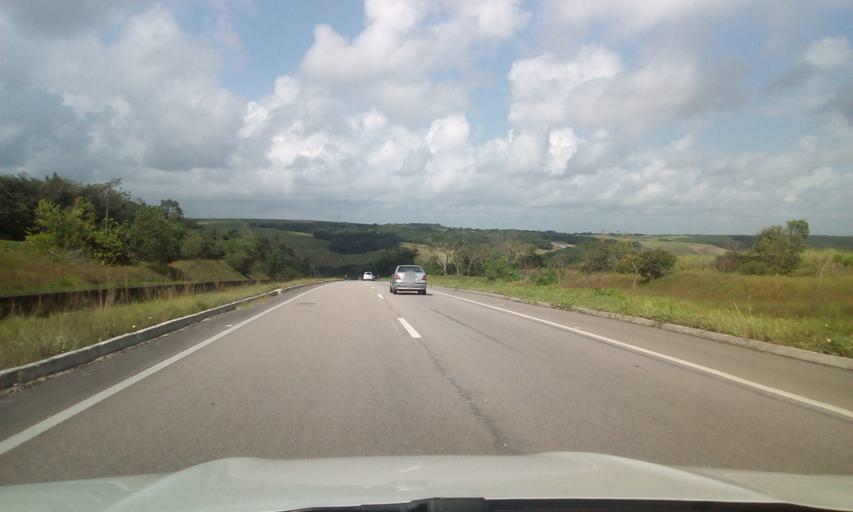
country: BR
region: Paraiba
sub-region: Alhandra
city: Alhandra
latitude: -7.4277
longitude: -34.9660
